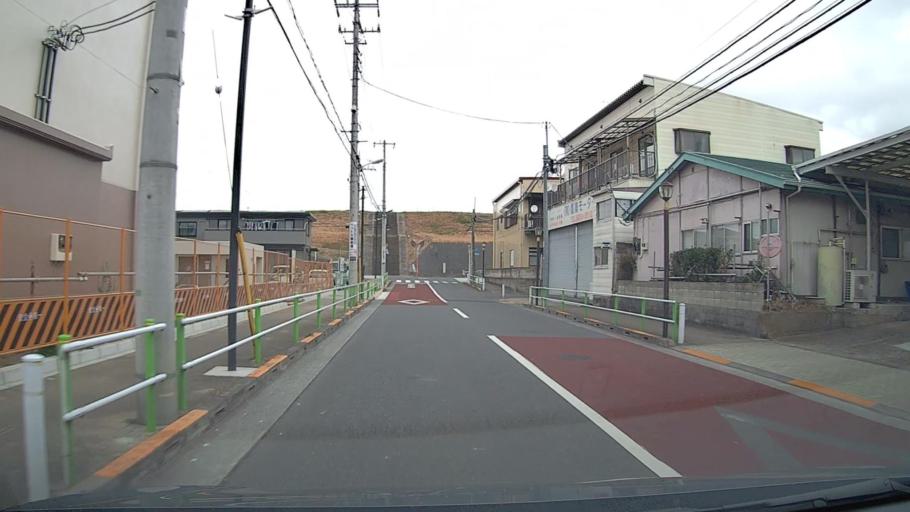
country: JP
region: Saitama
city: Shimotoda
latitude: 35.7968
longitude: 139.6642
